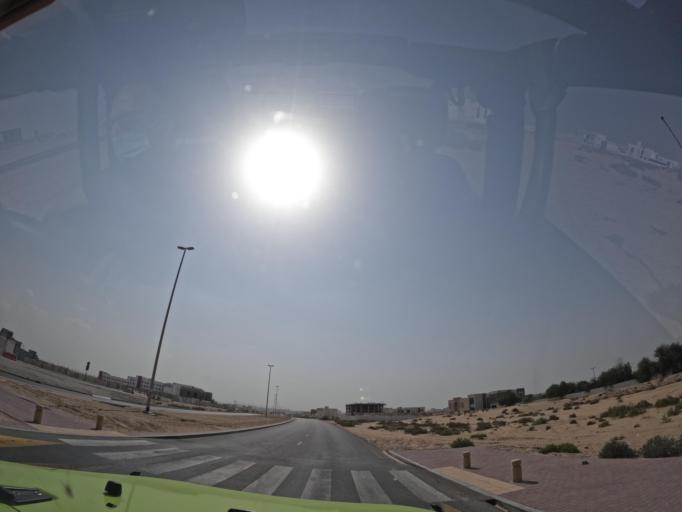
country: AE
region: Ash Shariqah
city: Sharjah
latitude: 25.1935
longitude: 55.4289
